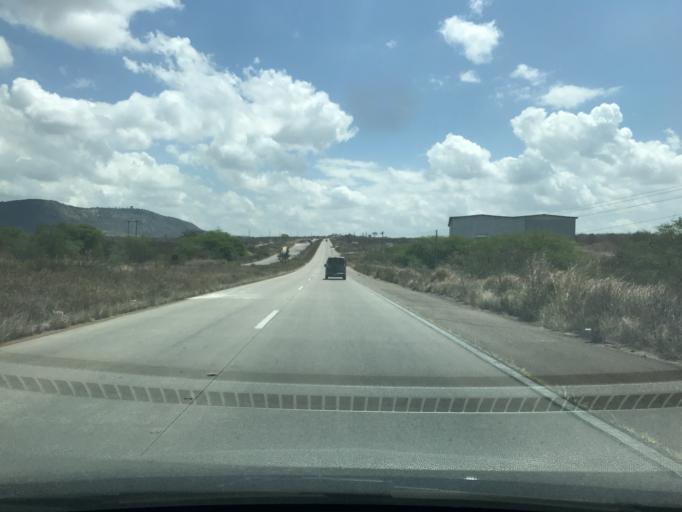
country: BR
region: Pernambuco
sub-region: Bezerros
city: Bezerros
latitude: -8.2900
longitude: -35.8217
